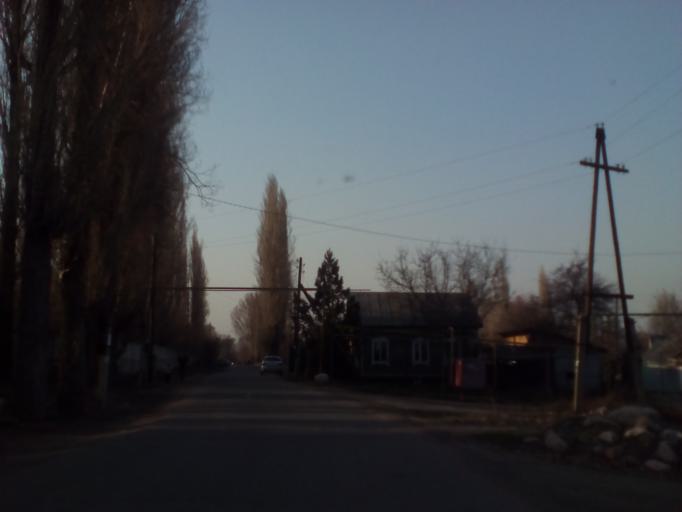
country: KZ
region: Almaty Oblysy
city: Burunday
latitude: 43.1545
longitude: 76.4228
